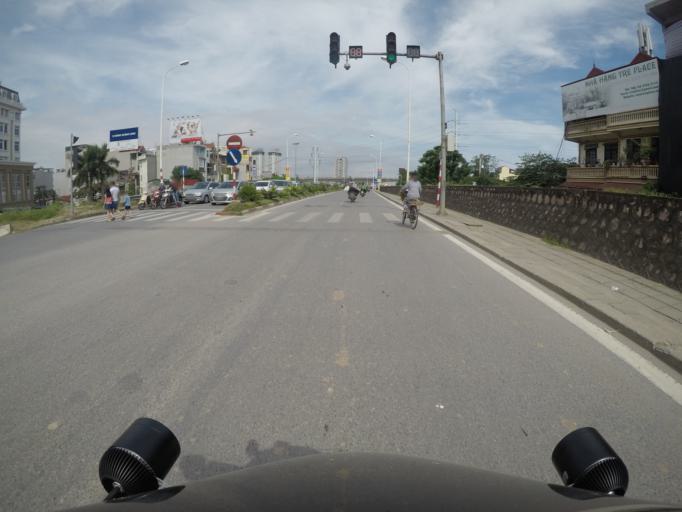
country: VN
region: Ha Noi
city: Tay Ho
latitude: 21.0813
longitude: 105.8181
